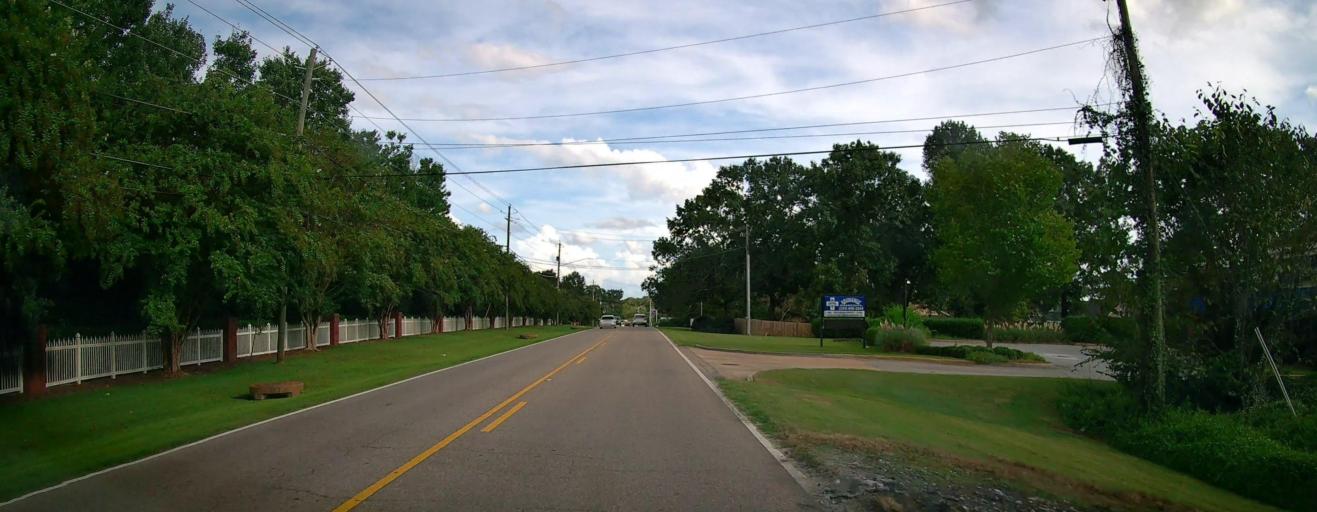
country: US
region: Alabama
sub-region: Russell County
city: Phenix City
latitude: 32.5145
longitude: -85.0237
